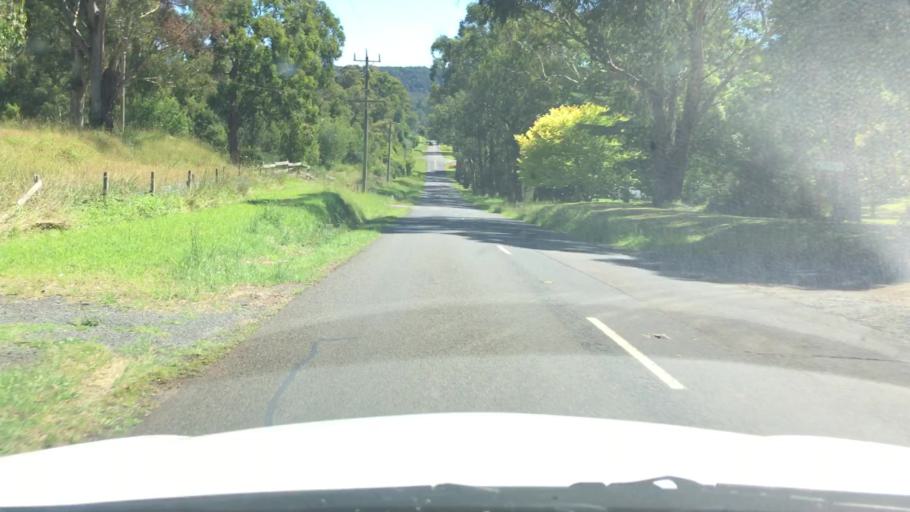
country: AU
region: Victoria
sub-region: Yarra Ranges
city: Mount Evelyn
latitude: -37.7988
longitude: 145.4214
